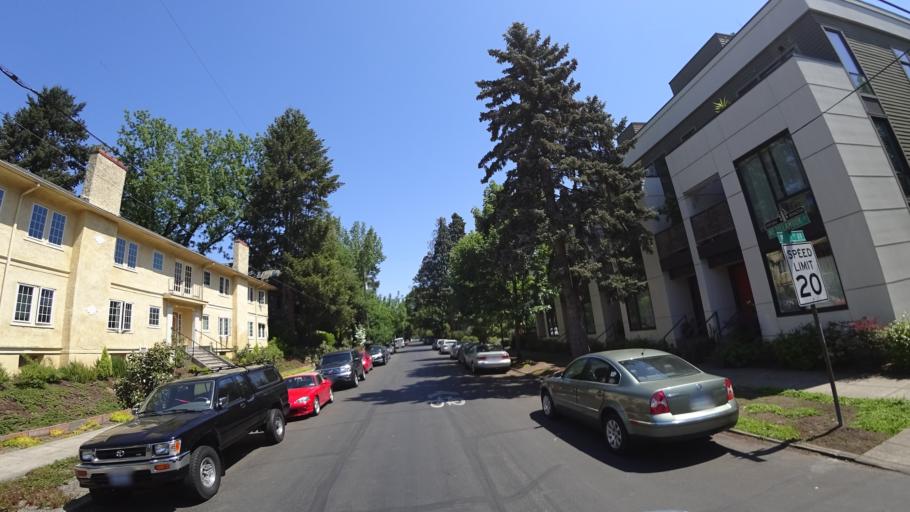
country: US
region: Oregon
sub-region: Multnomah County
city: Portland
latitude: 45.5375
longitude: -122.6545
